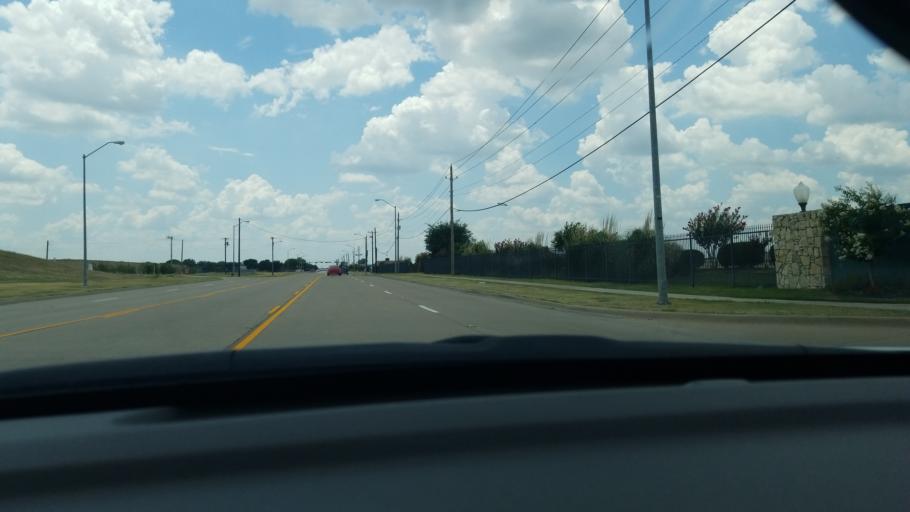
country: US
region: Texas
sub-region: Tarrant County
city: Arlington
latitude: 32.6916
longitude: -97.0506
